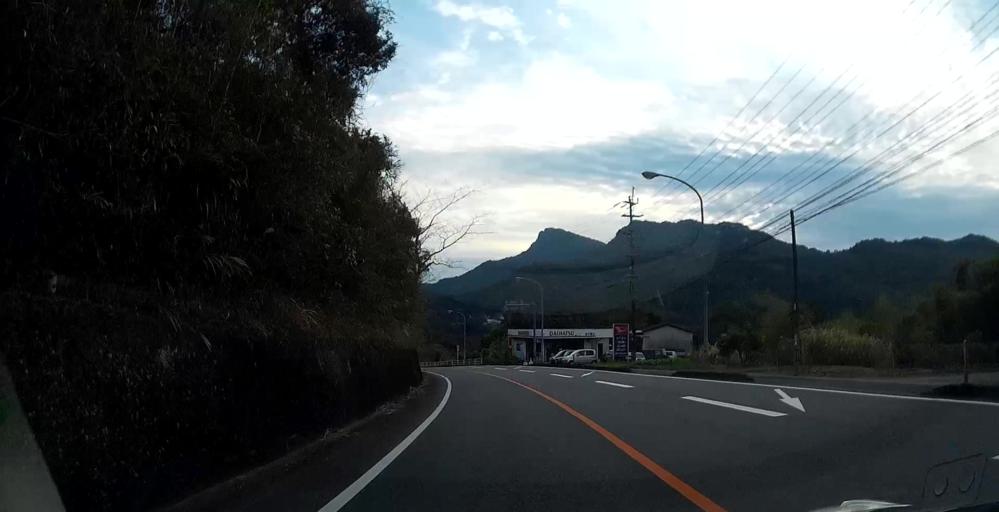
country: JP
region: Kumamoto
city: Yatsushiro
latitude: 32.4958
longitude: 130.4198
